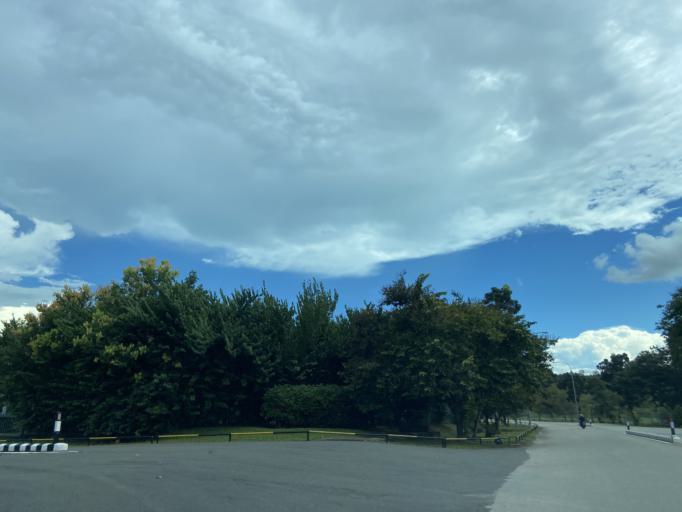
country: SG
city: Singapore
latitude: 1.0610
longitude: 104.0295
